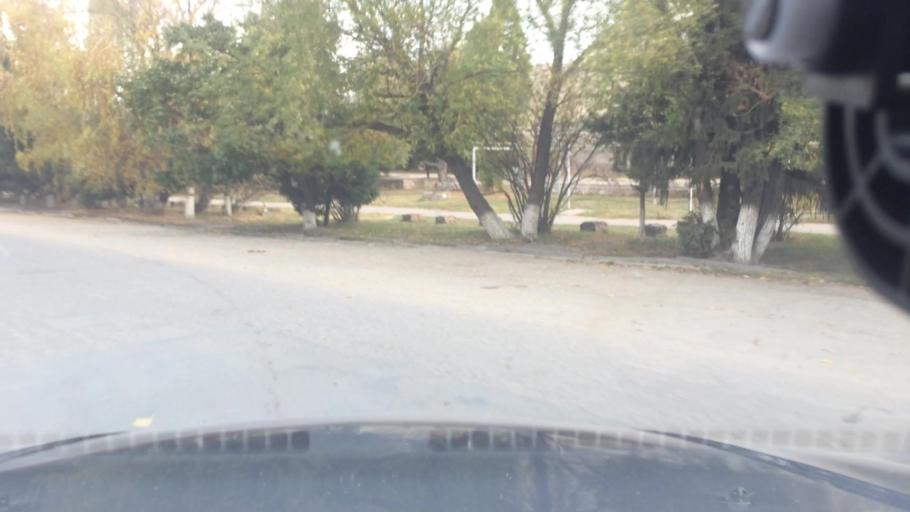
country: KG
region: Ysyk-Koel
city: Karakol
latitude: 42.4958
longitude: 78.3918
